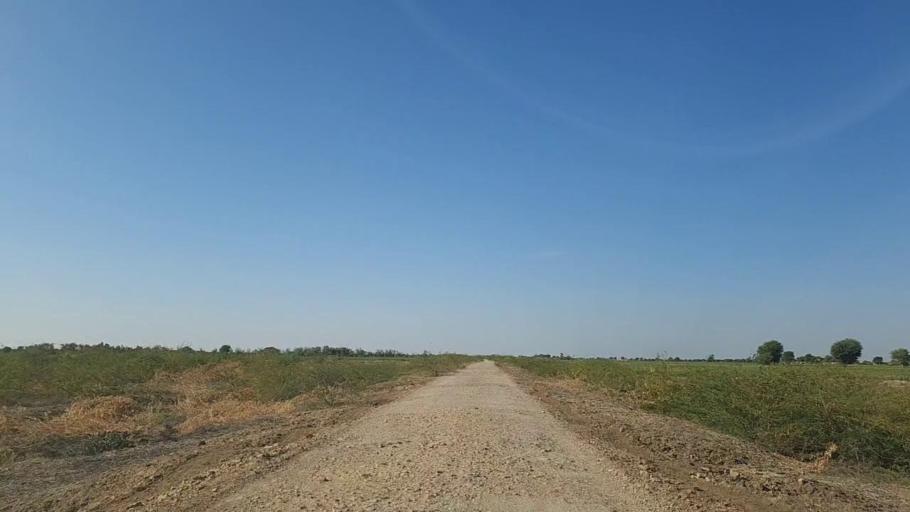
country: PK
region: Sindh
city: Kunri
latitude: 25.2452
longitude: 69.4965
